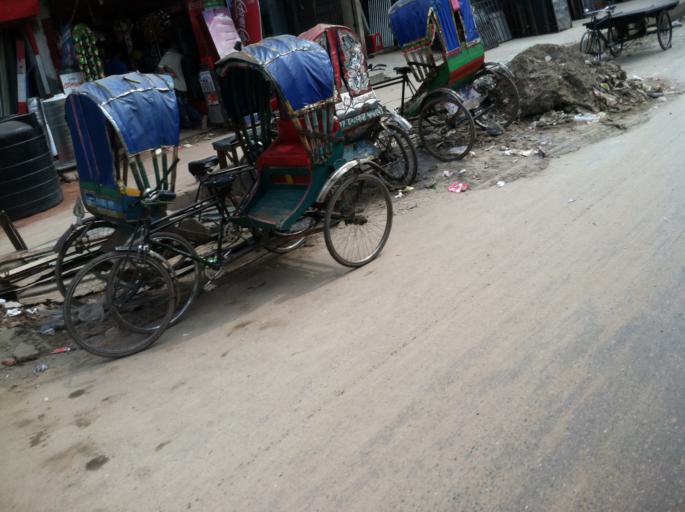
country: BD
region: Dhaka
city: Tungi
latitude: 23.8212
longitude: 90.3711
